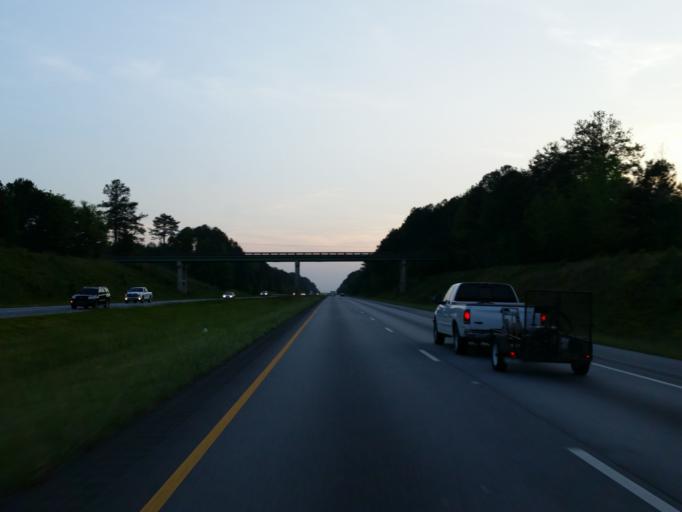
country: US
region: Alabama
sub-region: Cleburne County
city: Heflin
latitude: 33.6349
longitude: -85.5371
